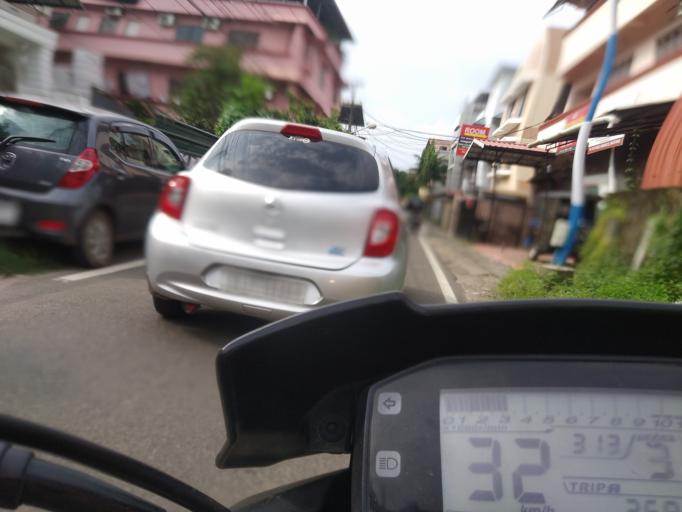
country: IN
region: Kerala
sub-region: Ernakulam
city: Cochin
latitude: 9.9738
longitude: 76.2873
